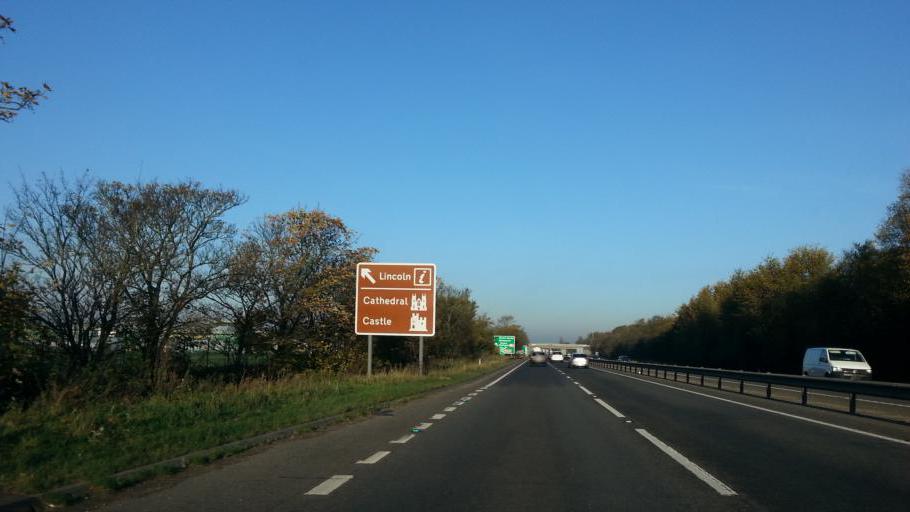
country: GB
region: England
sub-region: Nottinghamshire
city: Newark on Trent
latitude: 53.0901
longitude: -0.7825
